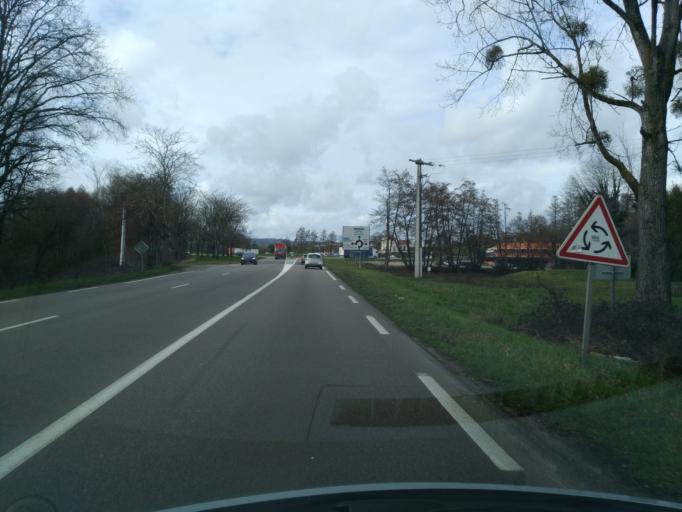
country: FR
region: Bourgogne
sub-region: Departement de Saone-et-Loire
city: Torcy
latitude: 46.7664
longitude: 4.4547
